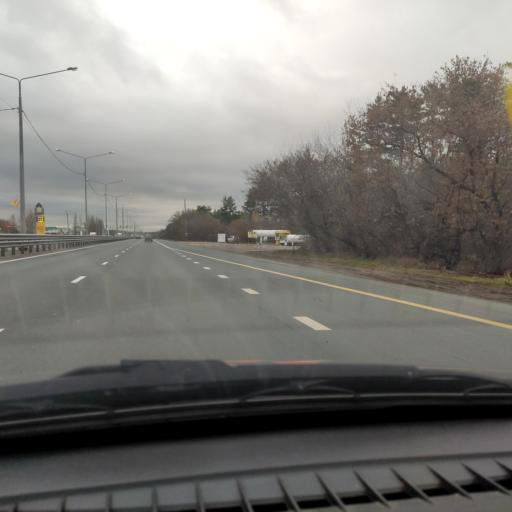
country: RU
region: Samara
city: Zhigulevsk
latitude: 53.5140
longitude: 49.6045
